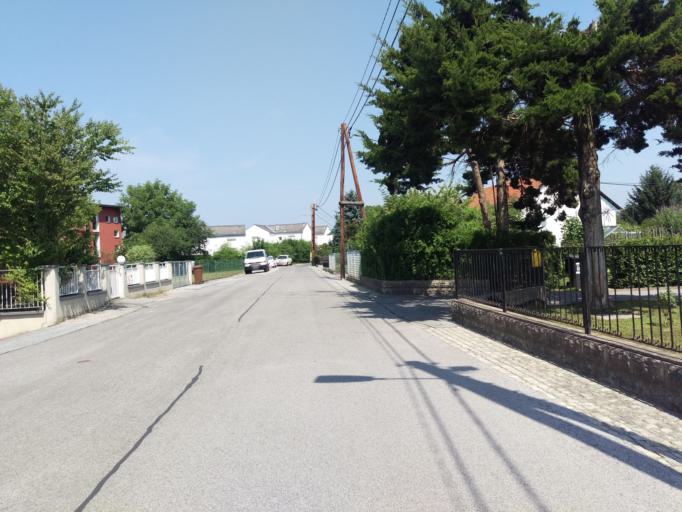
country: AT
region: Styria
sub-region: Politischer Bezirk Graz-Umgebung
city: Feldkirchen bei Graz
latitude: 47.0321
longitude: 15.4545
